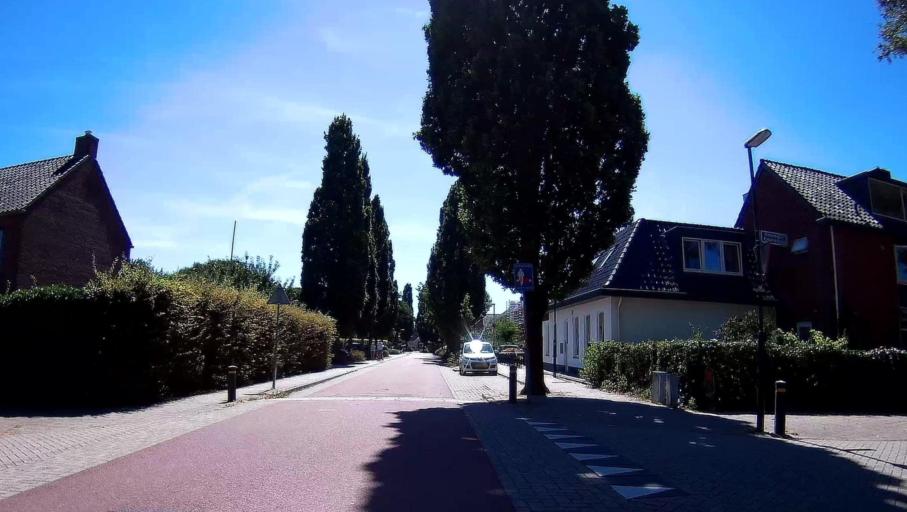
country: NL
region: Utrecht
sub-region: Gemeente Houten
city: Houten
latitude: 52.0301
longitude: 5.1673
